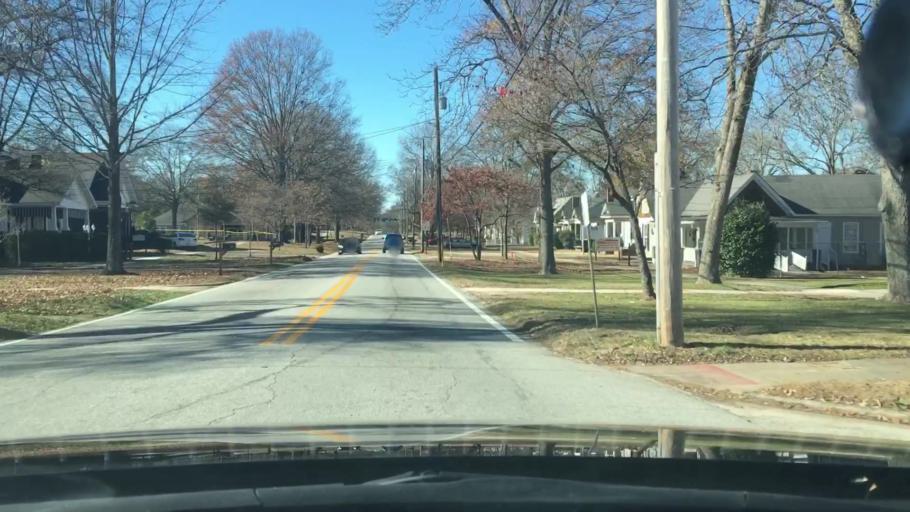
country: US
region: Georgia
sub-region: Spalding County
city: Griffin
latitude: 33.2488
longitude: -84.2705
